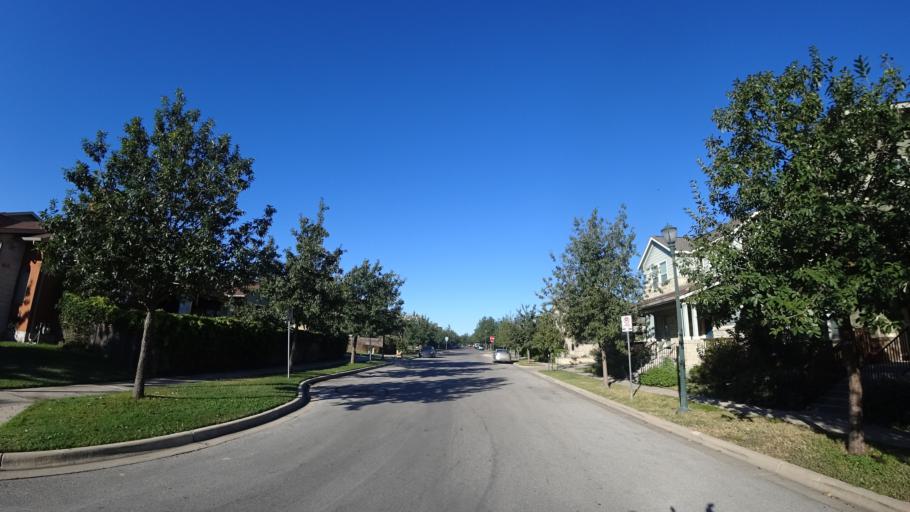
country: US
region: Texas
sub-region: Travis County
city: Austin
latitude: 30.2956
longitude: -97.7020
